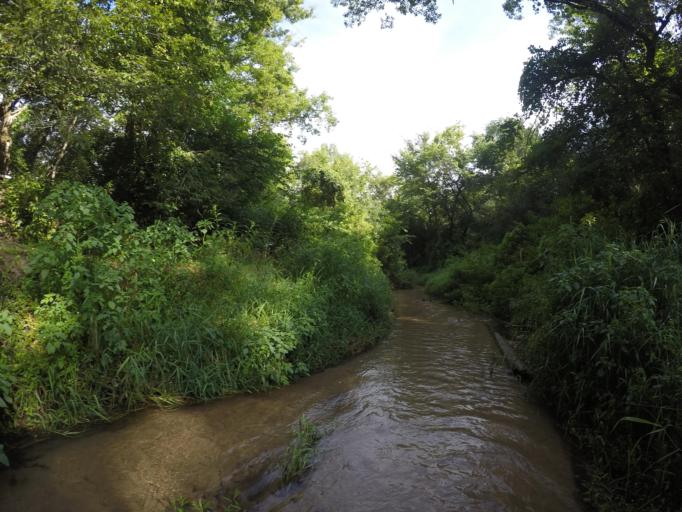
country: US
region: Minnesota
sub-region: Olmsted County
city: Eyota
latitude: 43.9810
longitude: -92.3394
